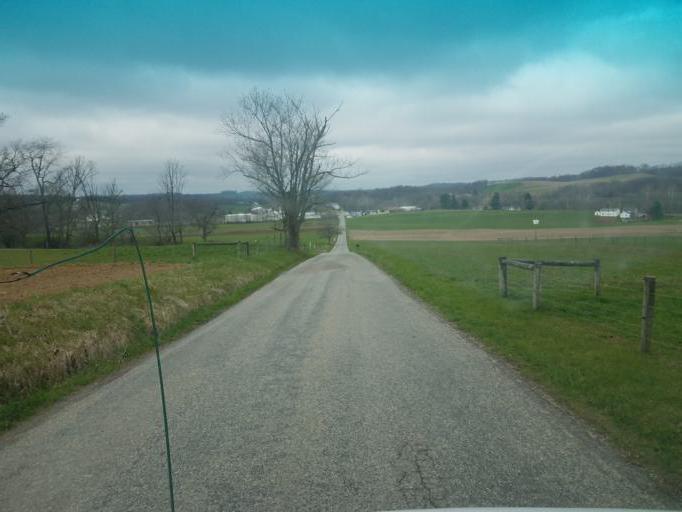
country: US
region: Ohio
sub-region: Stark County
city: Beach City
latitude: 40.6385
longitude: -81.6677
